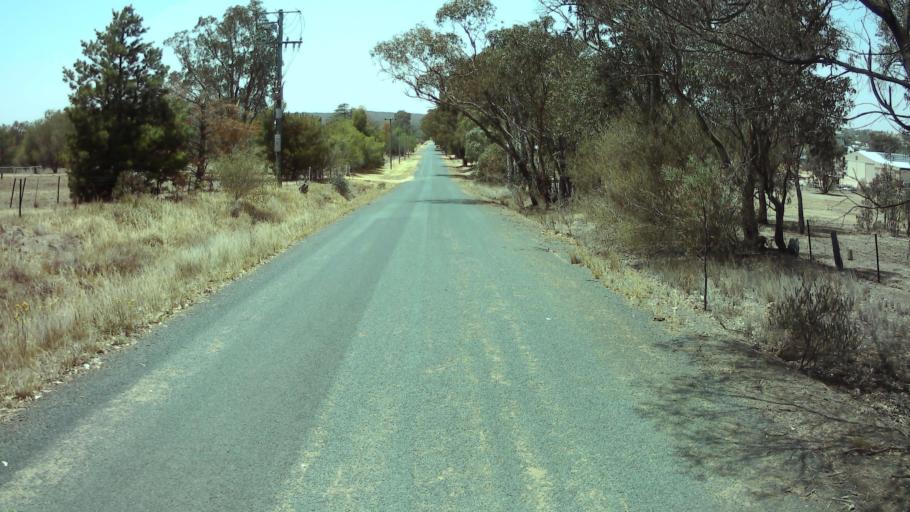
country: AU
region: New South Wales
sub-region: Weddin
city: Grenfell
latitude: -33.8887
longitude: 148.1483
